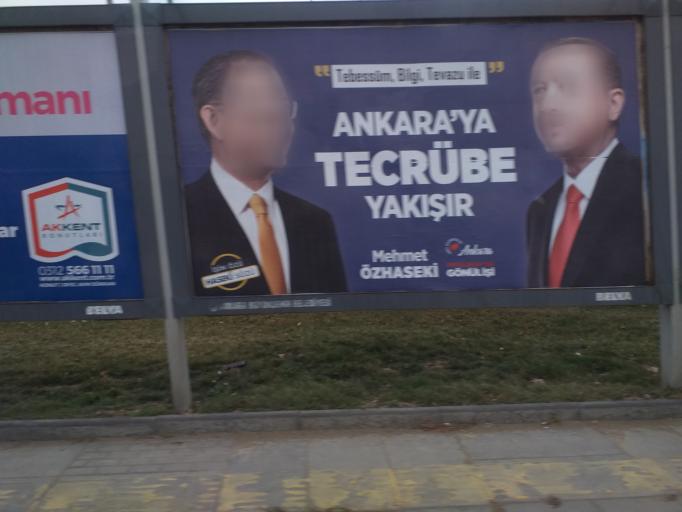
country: TR
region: Ankara
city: Ankara
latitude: 39.9513
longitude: 32.8233
